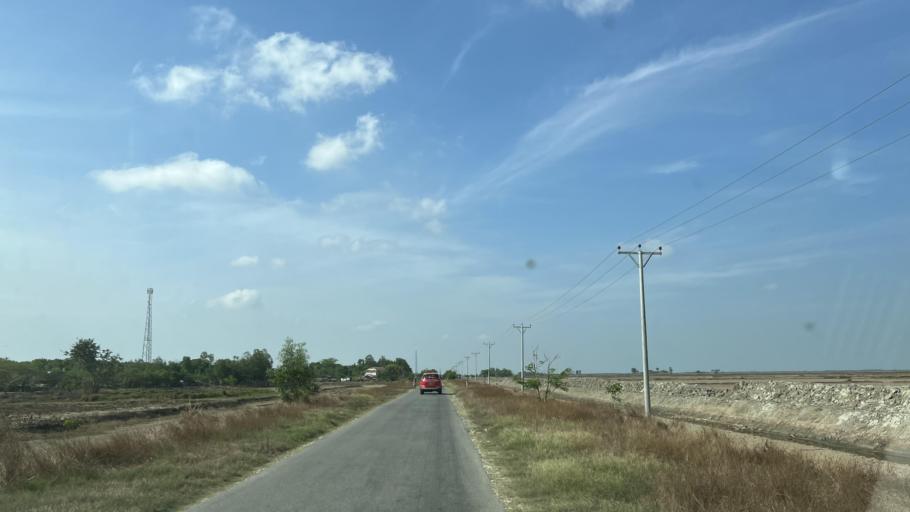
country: MM
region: Ayeyarwady
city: Pyapon
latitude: 15.9936
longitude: 95.5958
